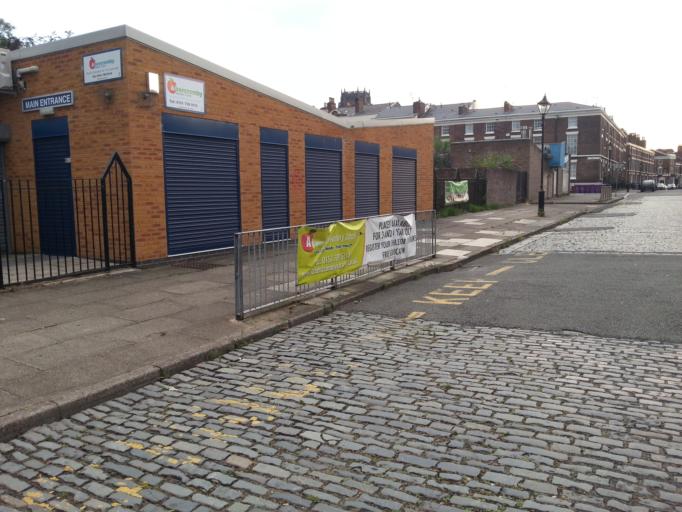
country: GB
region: England
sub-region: Liverpool
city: Liverpool
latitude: 53.3995
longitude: -2.9653
